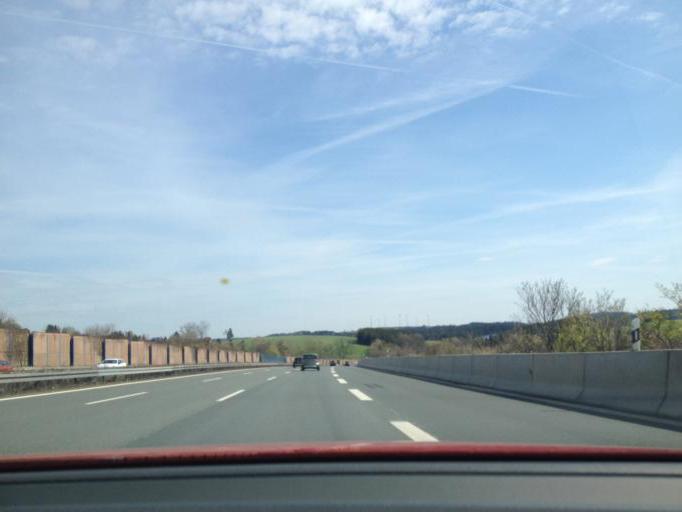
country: DE
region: Bavaria
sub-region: Upper Franconia
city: Gefrees
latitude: 50.1066
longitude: 11.7047
